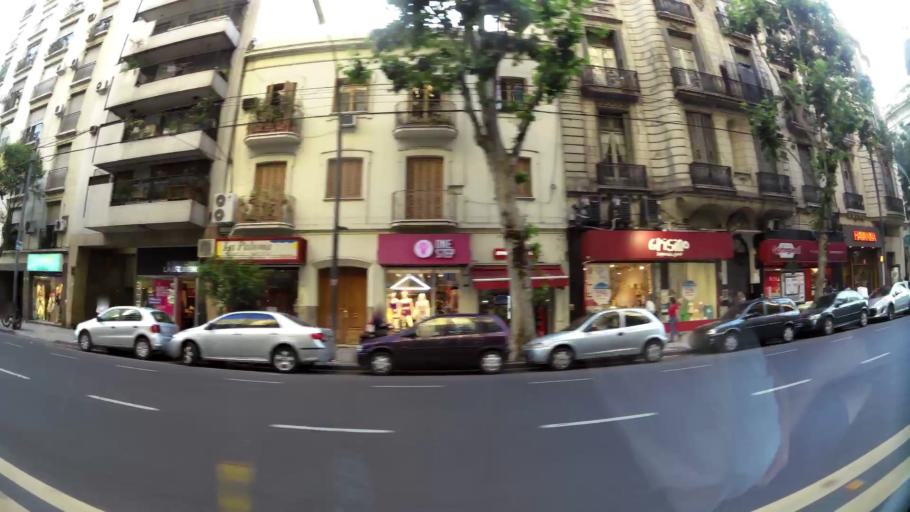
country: AR
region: Buenos Aires F.D.
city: Retiro
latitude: -34.5937
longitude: -58.4050
